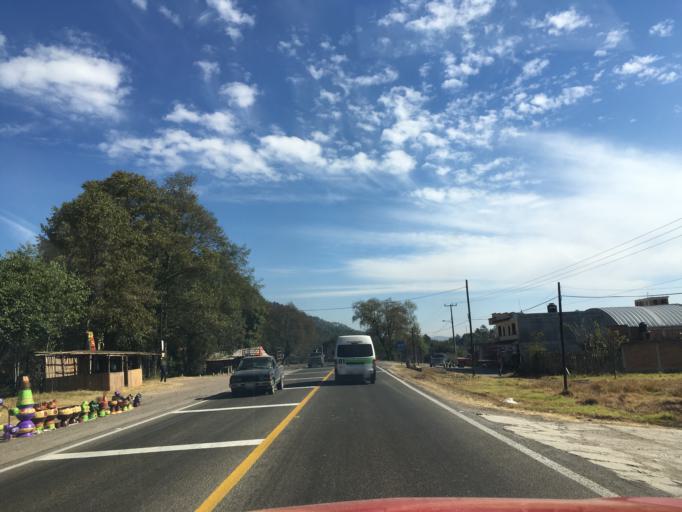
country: MX
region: Michoacan
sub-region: Hidalgo
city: San Lucas Huarirapeo (La Mesa de San Lucas)
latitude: 19.6719
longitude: -100.6661
